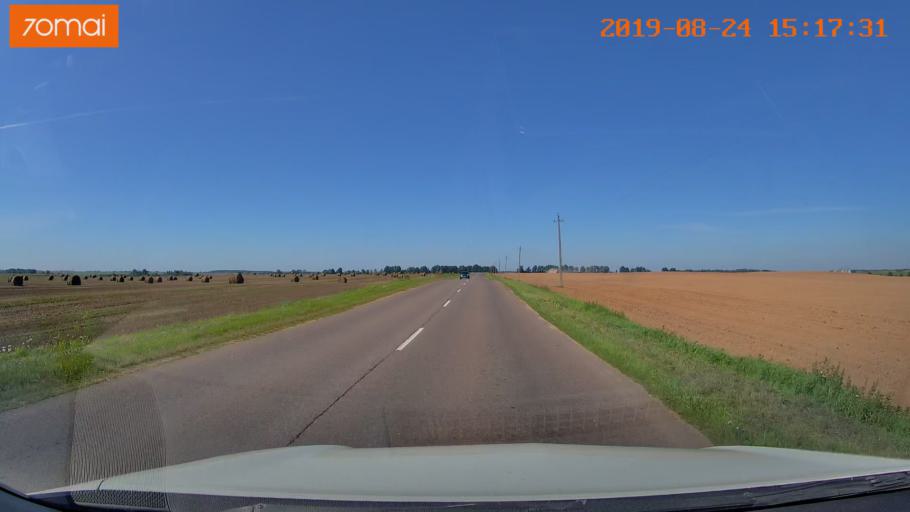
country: BY
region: Minsk
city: Samakhvalavichy
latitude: 53.6529
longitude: 27.5443
